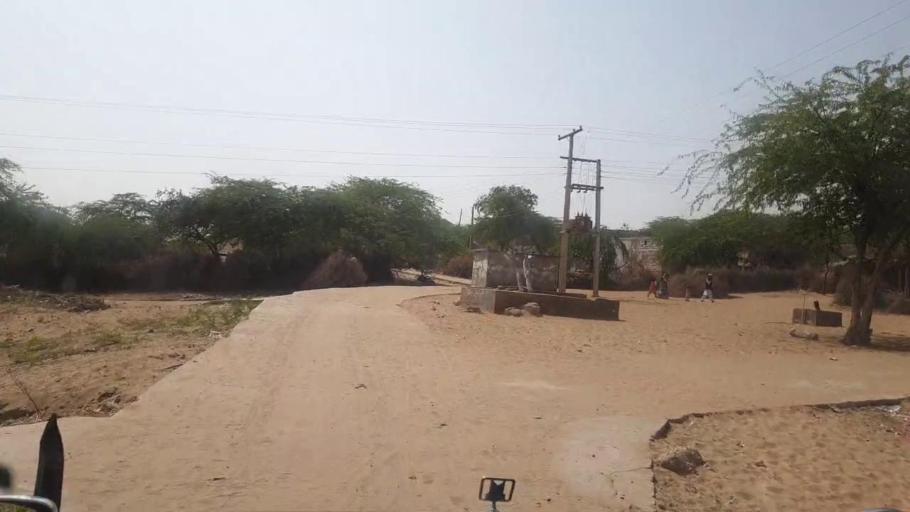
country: PK
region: Sindh
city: Islamkot
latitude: 25.1245
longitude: 70.2152
